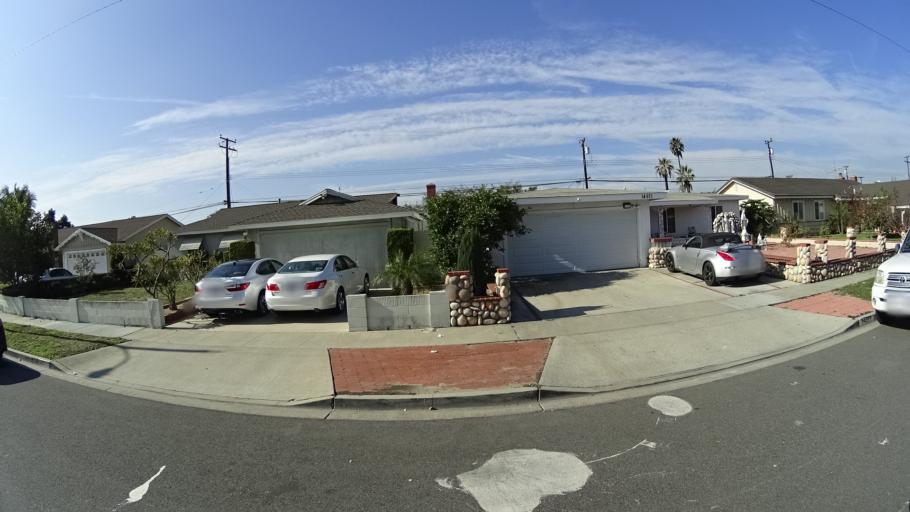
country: US
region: California
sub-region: Orange County
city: Midway City
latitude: 33.7509
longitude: -117.9762
